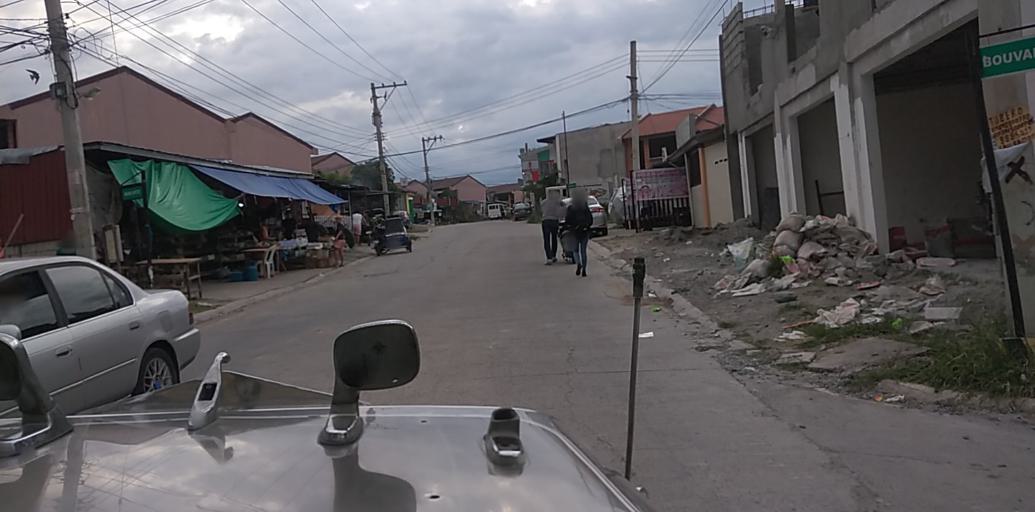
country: PH
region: Central Luzon
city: Santol
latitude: 15.1668
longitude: 120.5353
